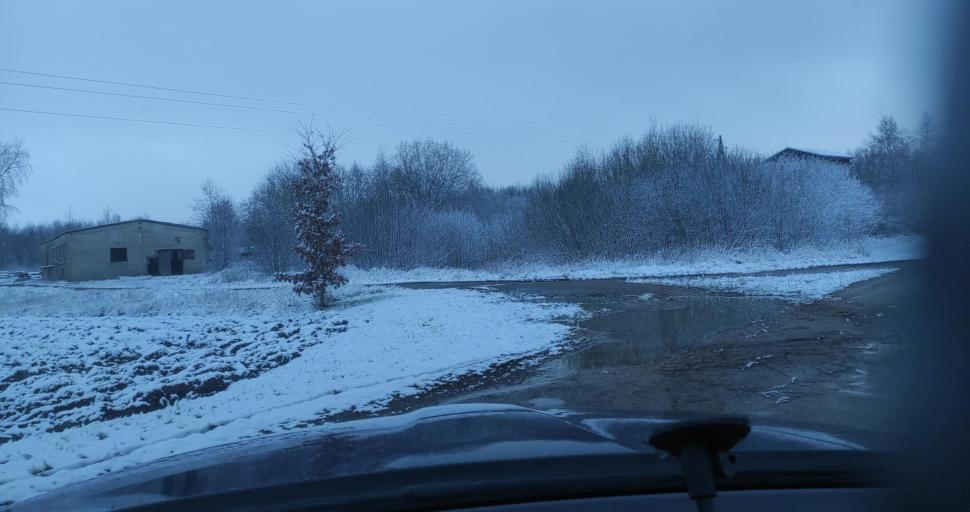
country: LV
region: Skrunda
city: Skrunda
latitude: 56.8692
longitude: 22.2405
